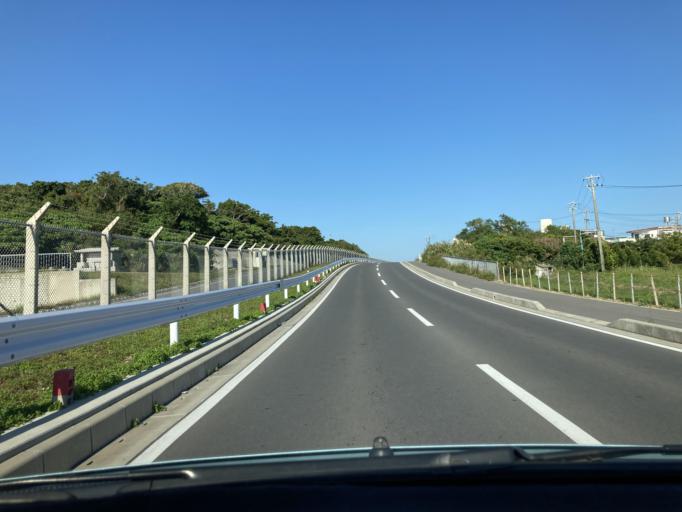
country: JP
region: Okinawa
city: Ginowan
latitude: 26.2687
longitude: 127.7617
